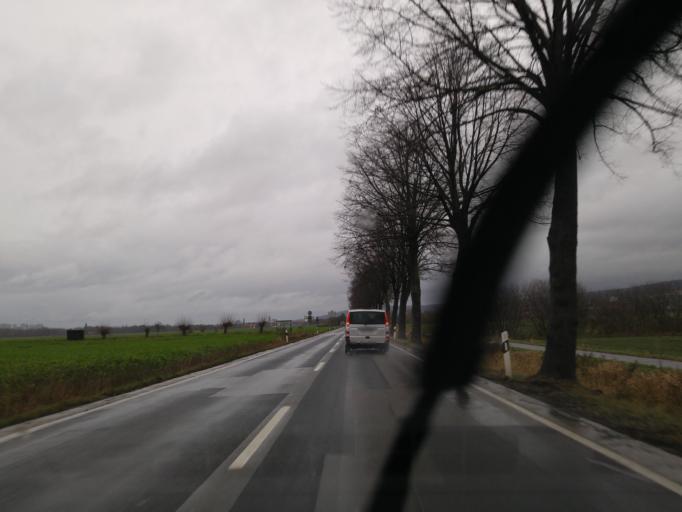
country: DE
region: Lower Saxony
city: Rosdorf
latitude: 51.4968
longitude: 9.9368
